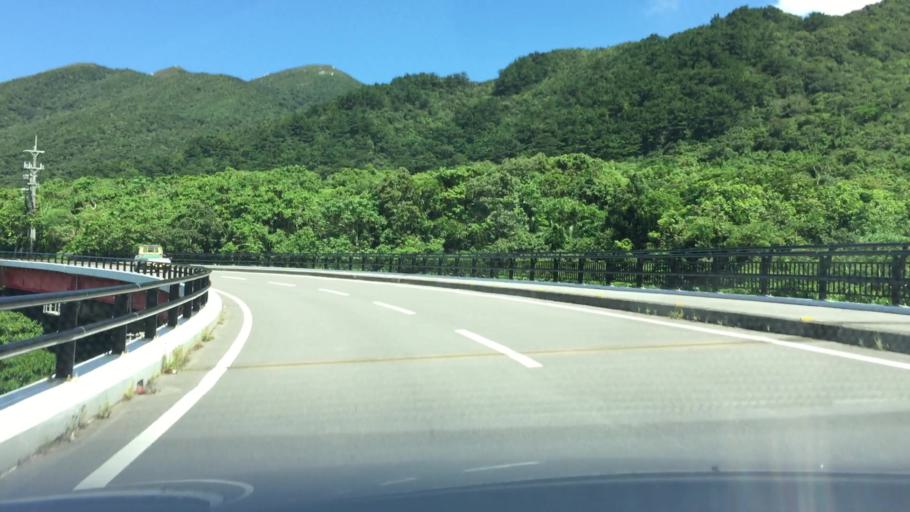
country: JP
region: Okinawa
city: Ishigaki
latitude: 24.4454
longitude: 124.1733
